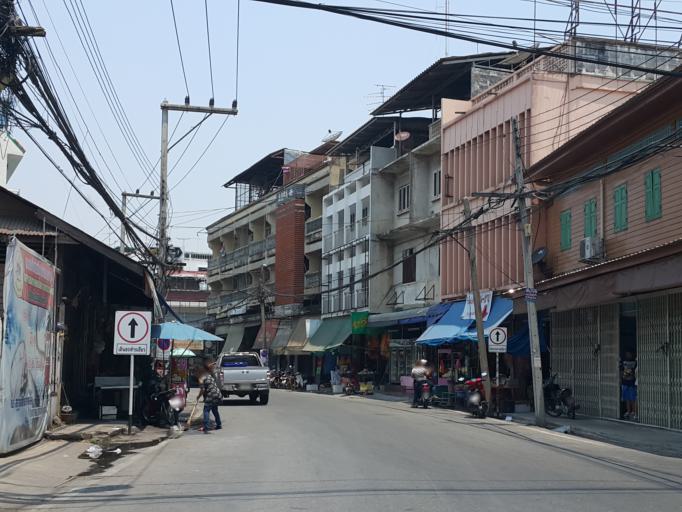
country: TH
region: Phitsanulok
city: Phitsanulok
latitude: 16.8168
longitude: 100.2630
